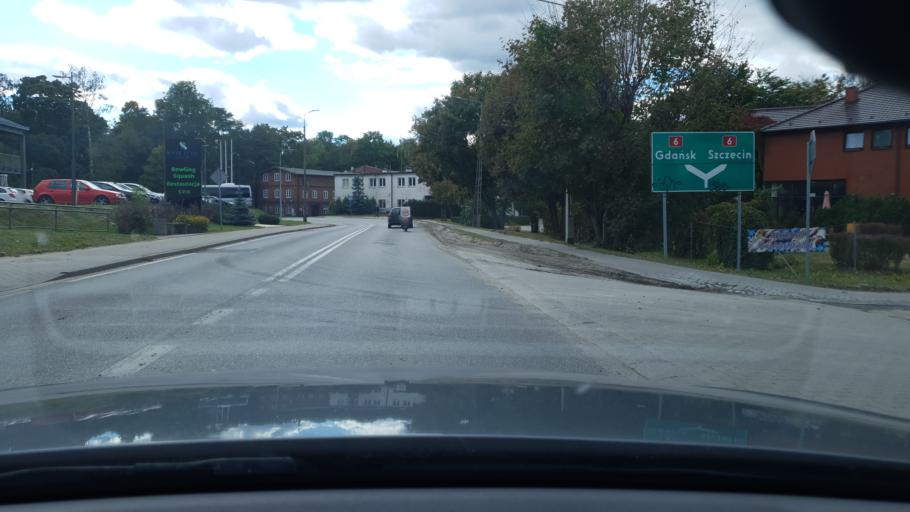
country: PL
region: Pomeranian Voivodeship
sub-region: Powiat wejherowski
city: Reda
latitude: 54.6084
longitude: 18.3486
